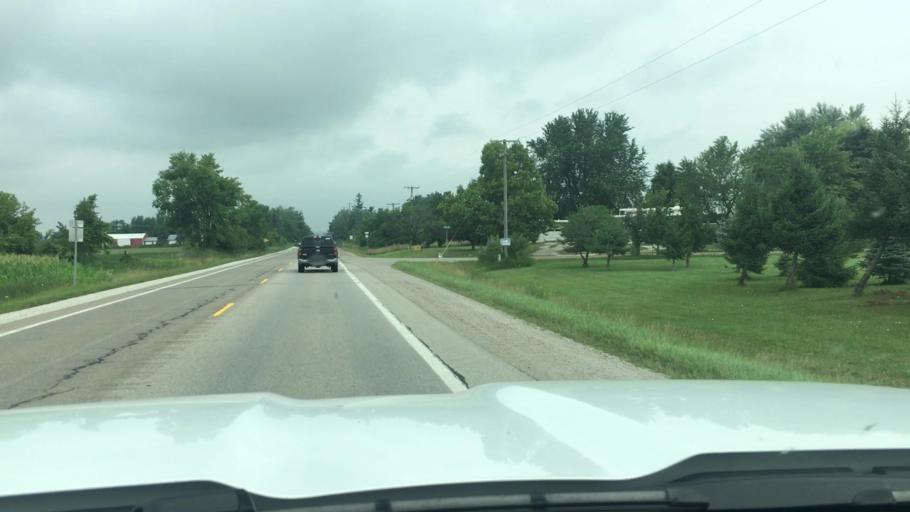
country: US
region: Michigan
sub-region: Sanilac County
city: Brown City
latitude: 43.1955
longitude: -83.0768
